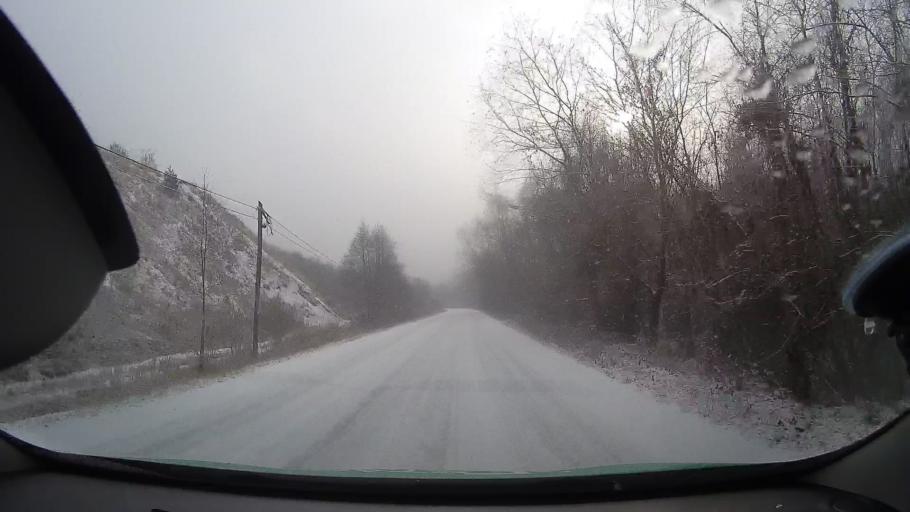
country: RO
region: Alba
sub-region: Comuna Livezile
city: Livezile
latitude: 46.3582
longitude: 23.6136
